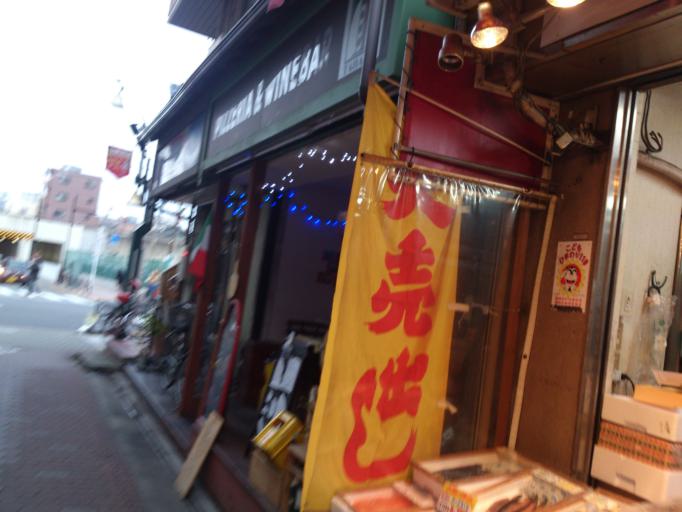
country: JP
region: Chiba
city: Matsudo
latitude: 35.7687
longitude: 139.8730
